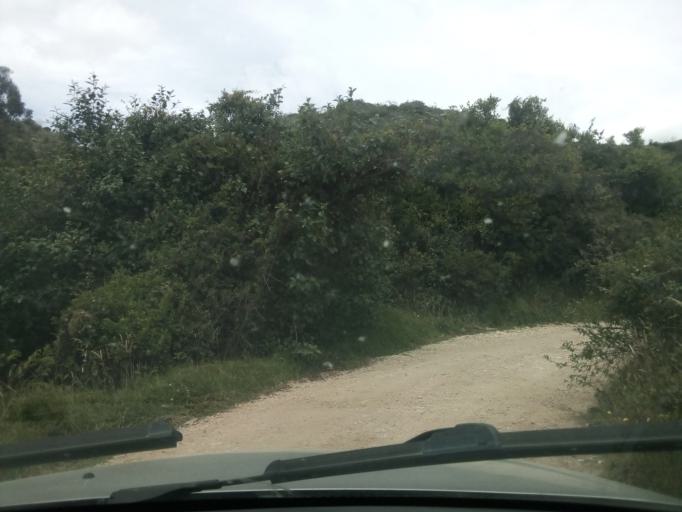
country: CO
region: Boyaca
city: Toca
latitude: 5.6206
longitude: -73.1243
